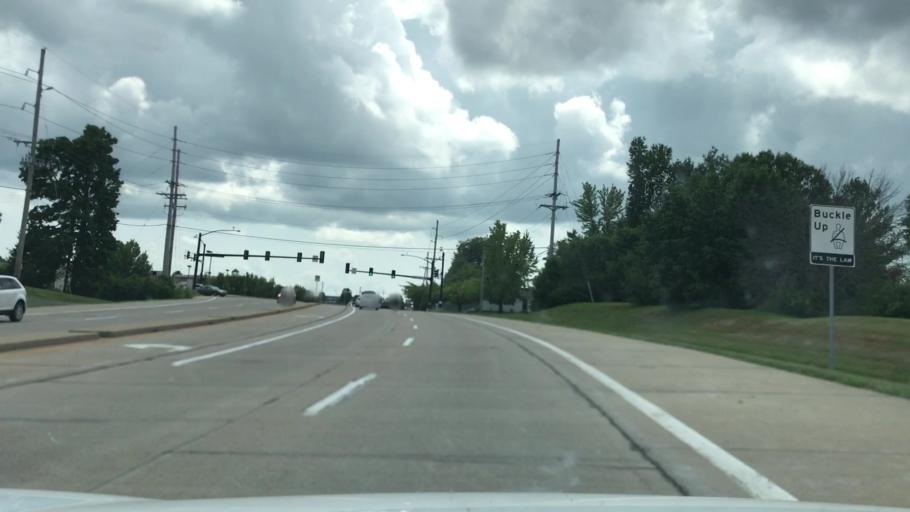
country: US
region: Missouri
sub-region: Saint Charles County
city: O'Fallon
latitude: 38.7884
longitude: -90.7000
